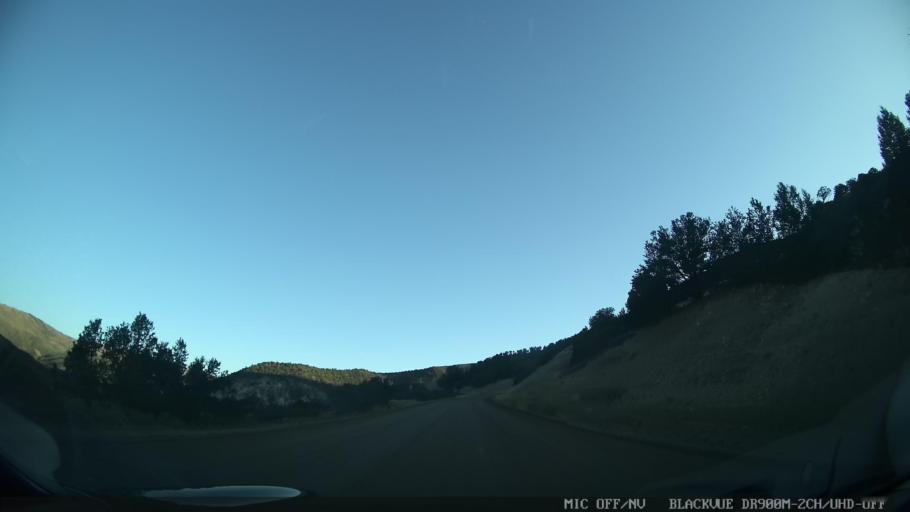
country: US
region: Colorado
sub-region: Grand County
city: Kremmling
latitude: 39.9398
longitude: -106.5286
